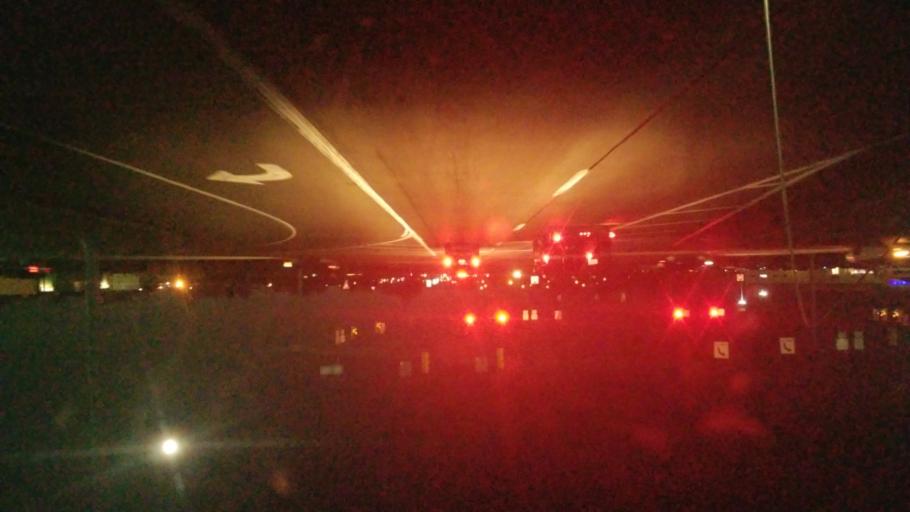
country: US
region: Indiana
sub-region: Decatur County
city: Greensburg
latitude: 39.3477
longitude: -85.4982
